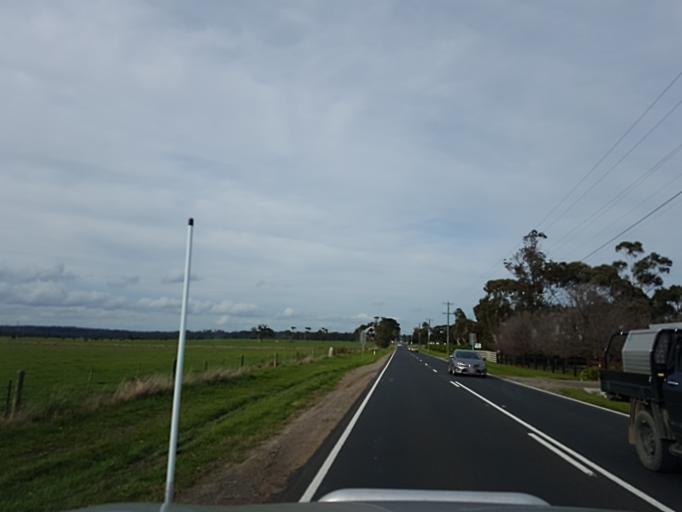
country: AU
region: Victoria
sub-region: Mornington Peninsula
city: Moorooduc
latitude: -38.2484
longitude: 145.1078
